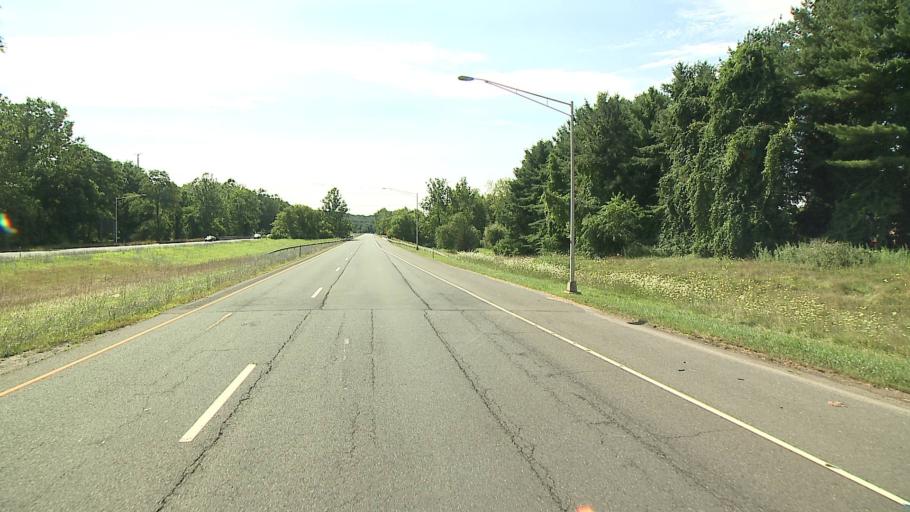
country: US
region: Connecticut
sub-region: Fairfield County
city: Danbury
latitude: 41.4675
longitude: -73.4043
